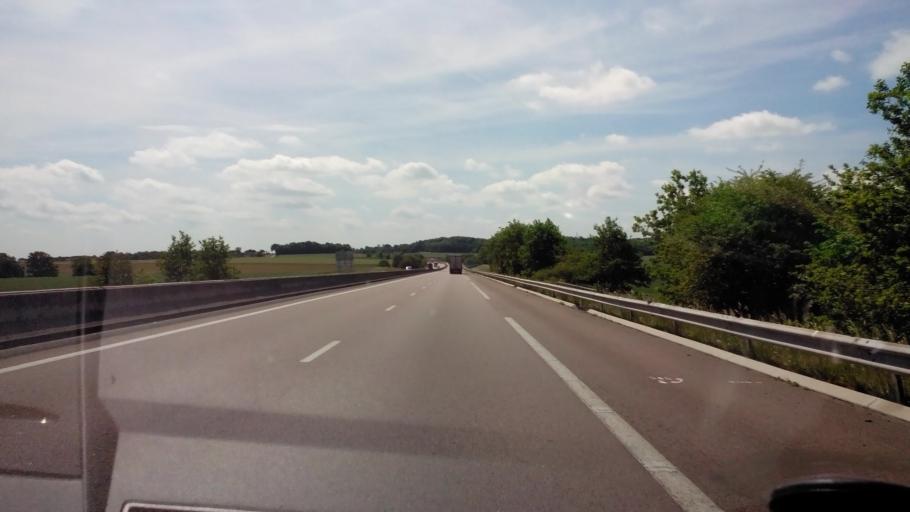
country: FR
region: Lorraine
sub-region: Departement de Meurthe-et-Moselle
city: Colombey-les-Belles
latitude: 48.4197
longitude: 5.8622
